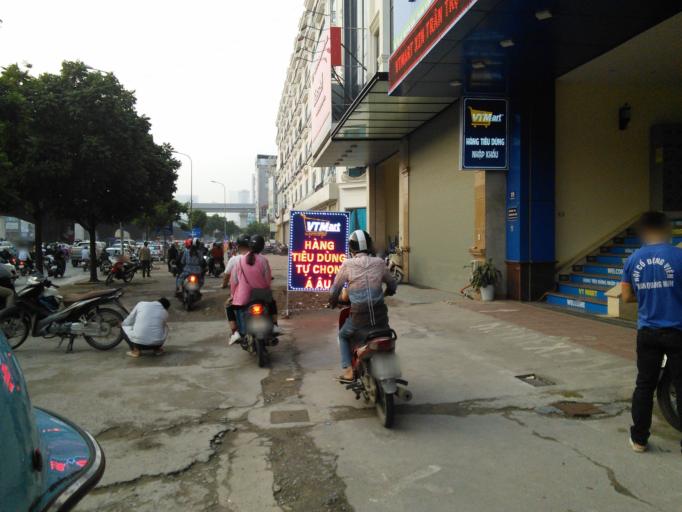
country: VN
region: Ha Noi
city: Thanh Xuan
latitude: 20.9898
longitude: 105.8049
